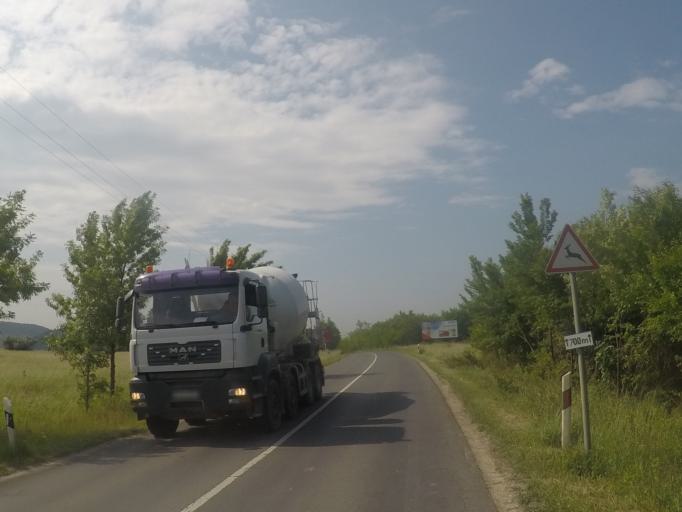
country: HU
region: Pest
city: Budakeszi
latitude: 47.4858
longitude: 18.9059
